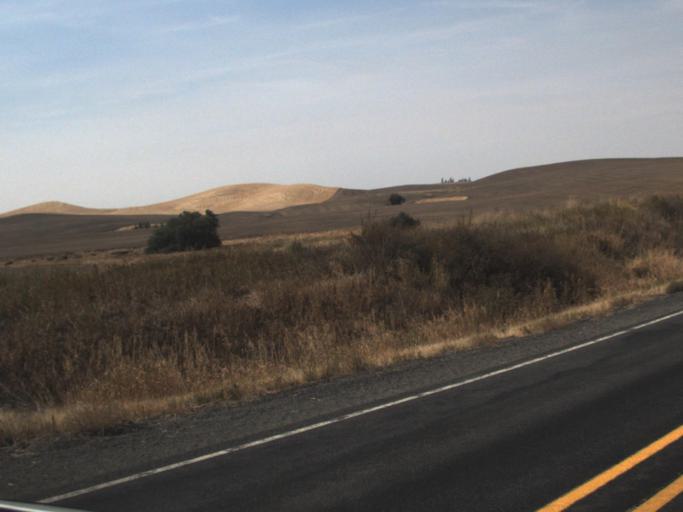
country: US
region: Idaho
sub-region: Benewah County
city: Plummer
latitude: 47.2340
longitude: -117.1153
